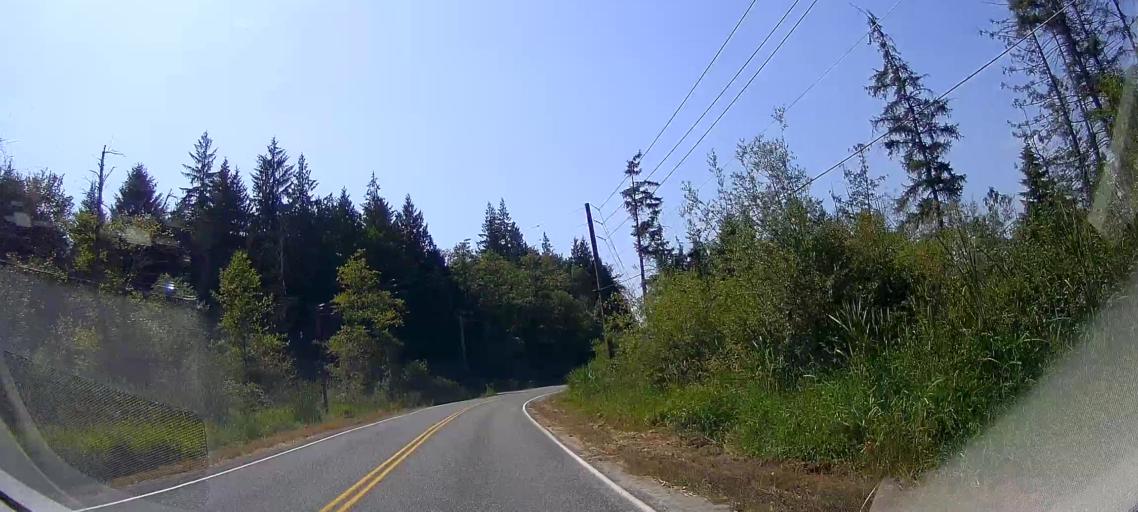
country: US
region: Washington
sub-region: Snohomish County
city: Bryant
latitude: 48.3269
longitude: -122.1521
